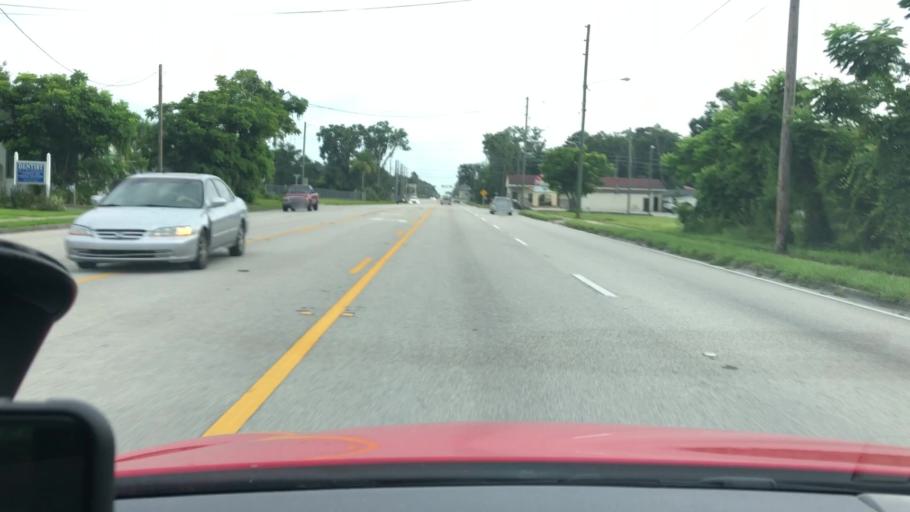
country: US
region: Florida
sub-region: Volusia County
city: West DeLand
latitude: 29.0299
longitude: -81.3242
